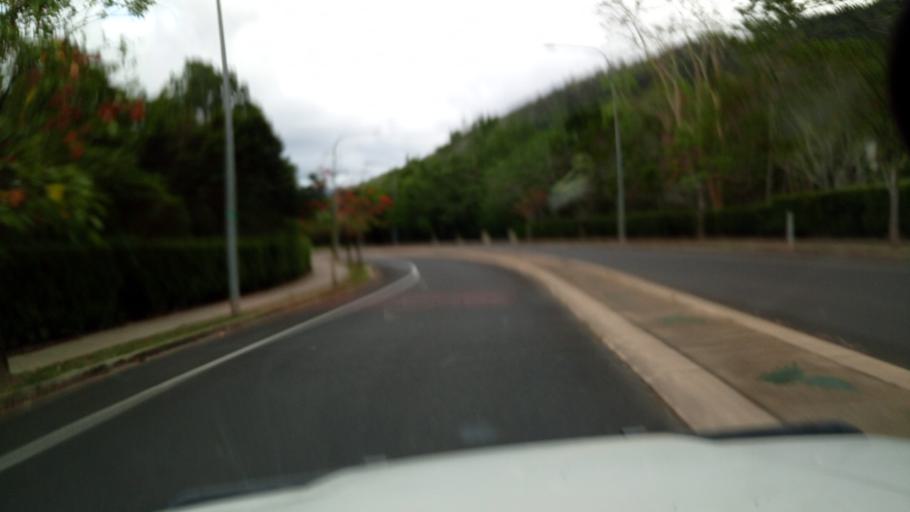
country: AU
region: Queensland
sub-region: Cairns
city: Redlynch
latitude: -16.8395
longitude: 145.6894
